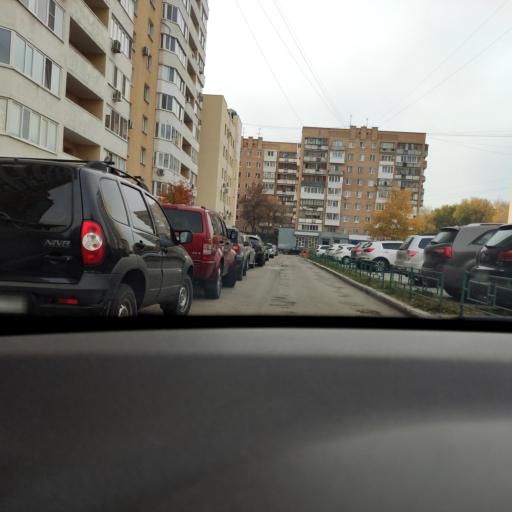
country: RU
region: Samara
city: Samara
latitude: 53.2488
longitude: 50.2376
